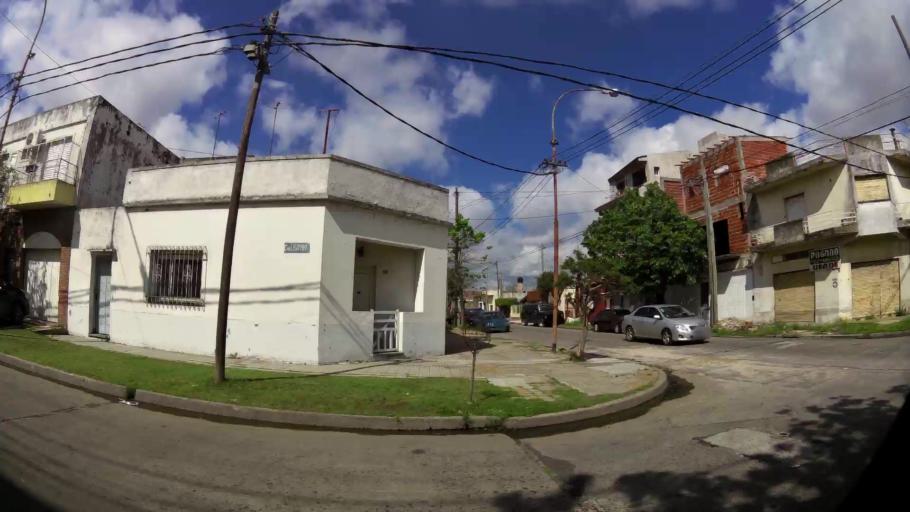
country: AR
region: Buenos Aires
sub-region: Partido de Lanus
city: Lanus
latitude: -34.6912
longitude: -58.4104
